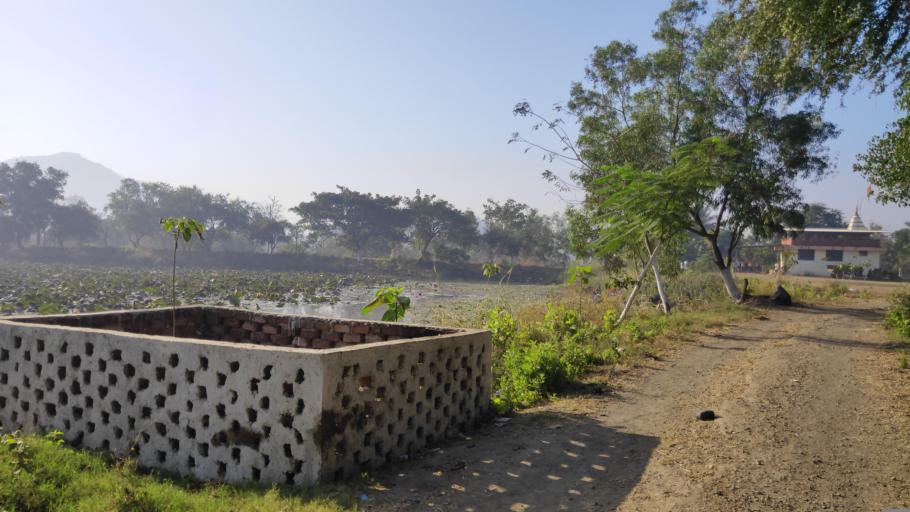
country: IN
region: Maharashtra
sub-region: Thane
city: Bhiwandi
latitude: 19.3274
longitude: 72.9776
